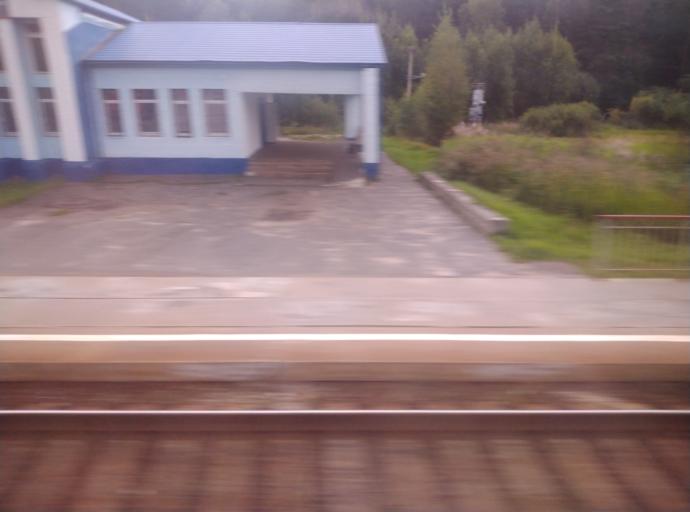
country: RU
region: Jaroslavl
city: Yaroslavl
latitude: 57.5277
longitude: 39.9610
